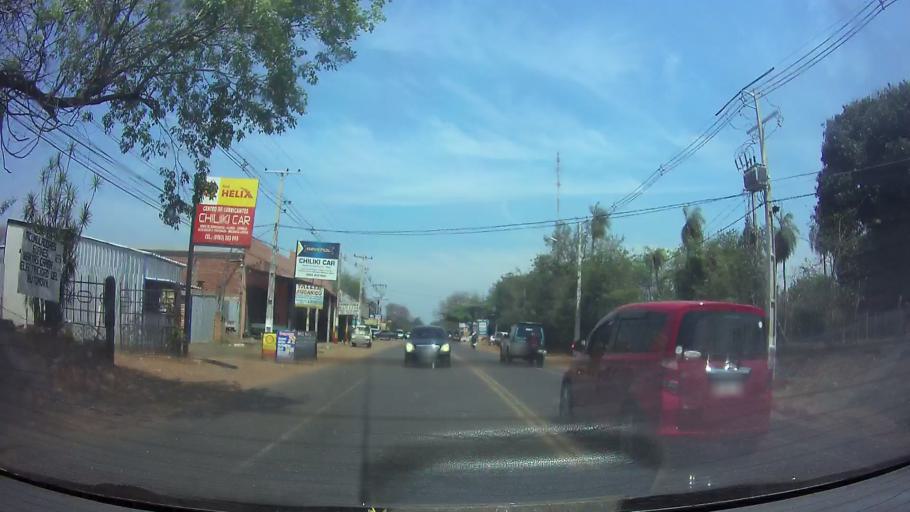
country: PY
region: Central
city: Capiata
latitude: -25.4007
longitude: -57.4645
